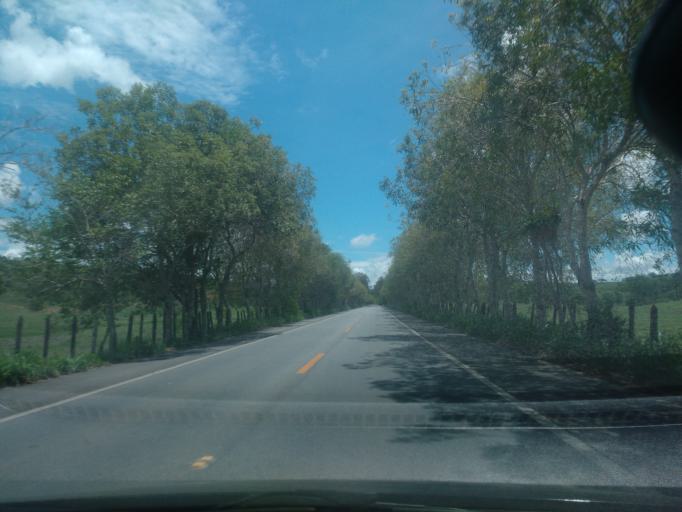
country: BR
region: Alagoas
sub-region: Uniao Dos Palmares
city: Uniao dos Palmares
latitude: -9.1462
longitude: -36.0150
